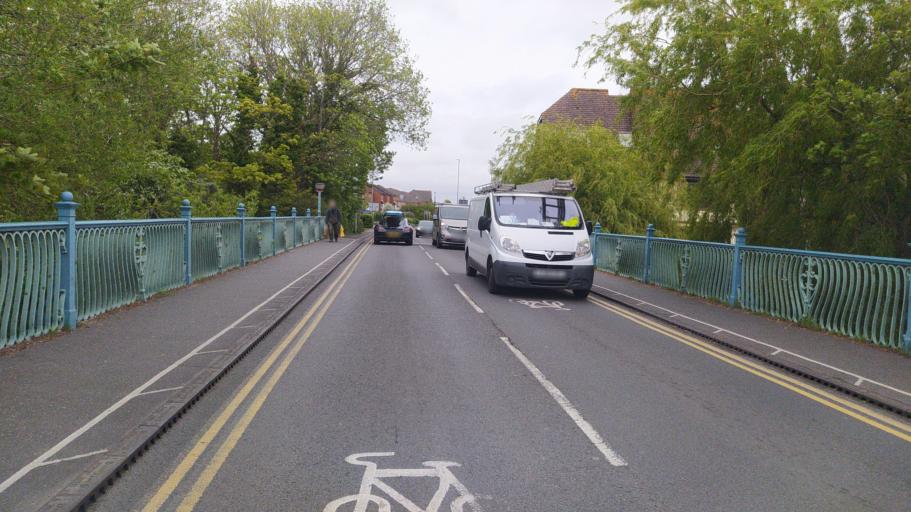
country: GB
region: England
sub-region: Dorset
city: Christchurch
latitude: 50.7301
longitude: -1.7896
